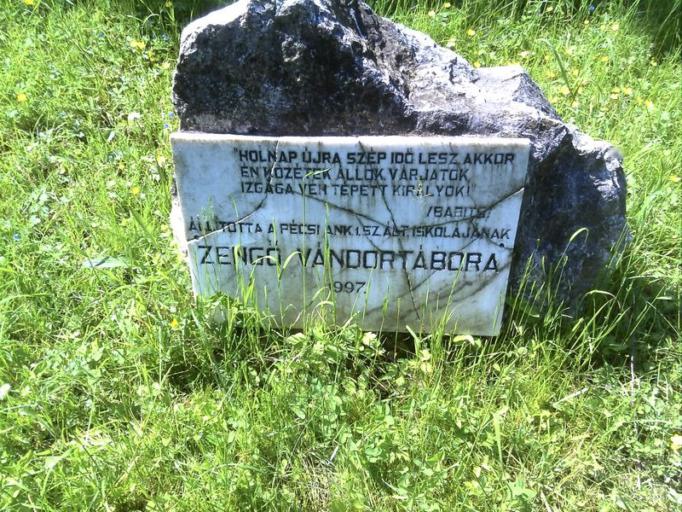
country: HU
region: Baranya
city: Hosszuheteny
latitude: 46.1855
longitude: 18.3815
